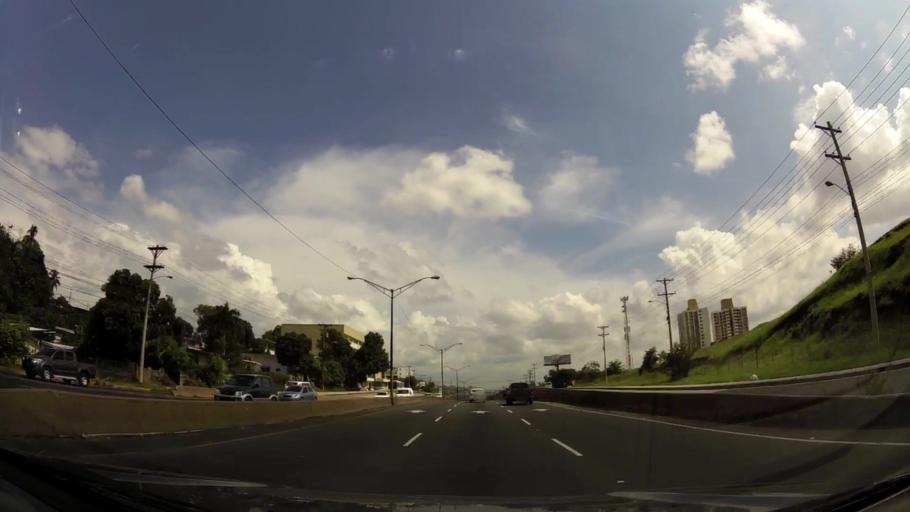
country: PA
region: Panama
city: San Miguelito
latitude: 9.0298
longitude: -79.4926
